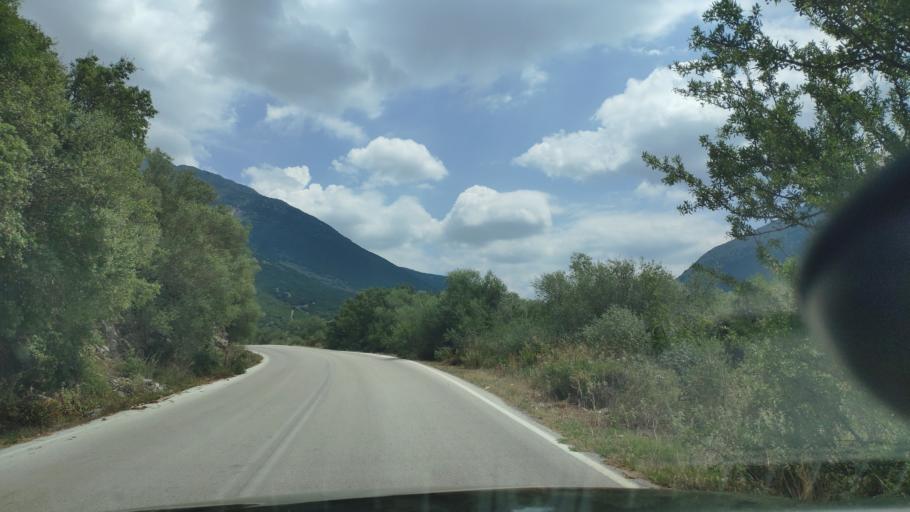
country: GR
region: Epirus
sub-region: Nomos Artas
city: Kampi
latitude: 39.2684
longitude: 20.9288
